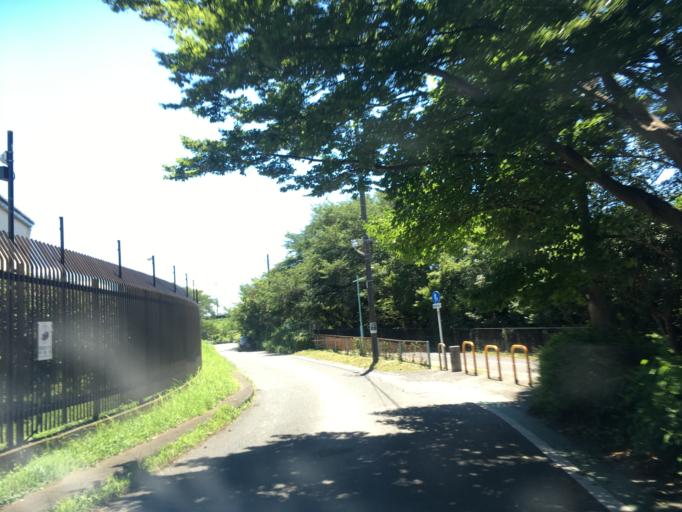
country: JP
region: Tokyo
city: Higashimurayama-shi
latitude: 35.7515
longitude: 139.4532
